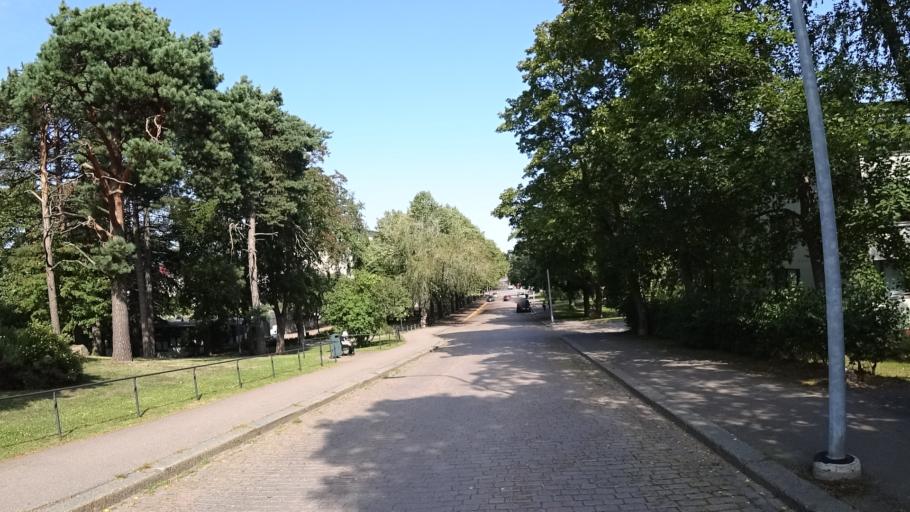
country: FI
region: Kymenlaakso
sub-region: Kotka-Hamina
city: Kotka
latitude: 60.4613
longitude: 26.9331
